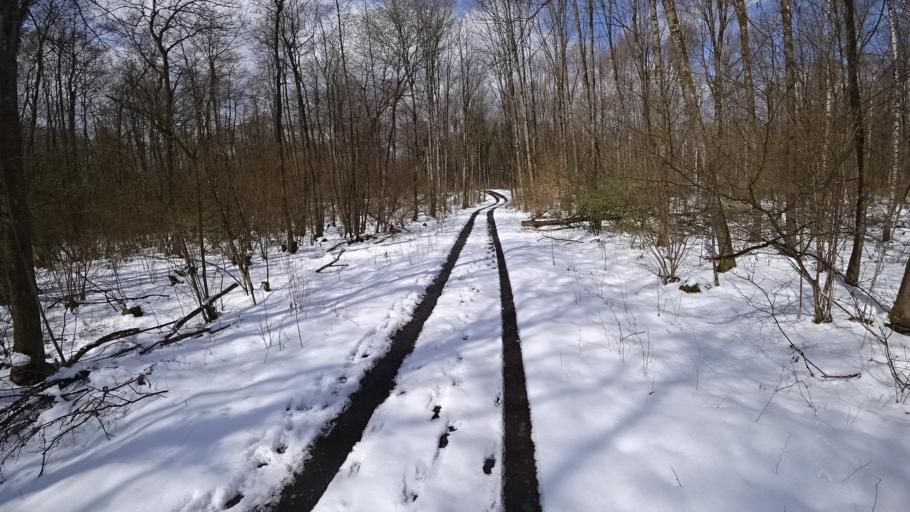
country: DE
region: Rheinland-Pfalz
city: Kausen
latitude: 50.7267
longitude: 7.8685
